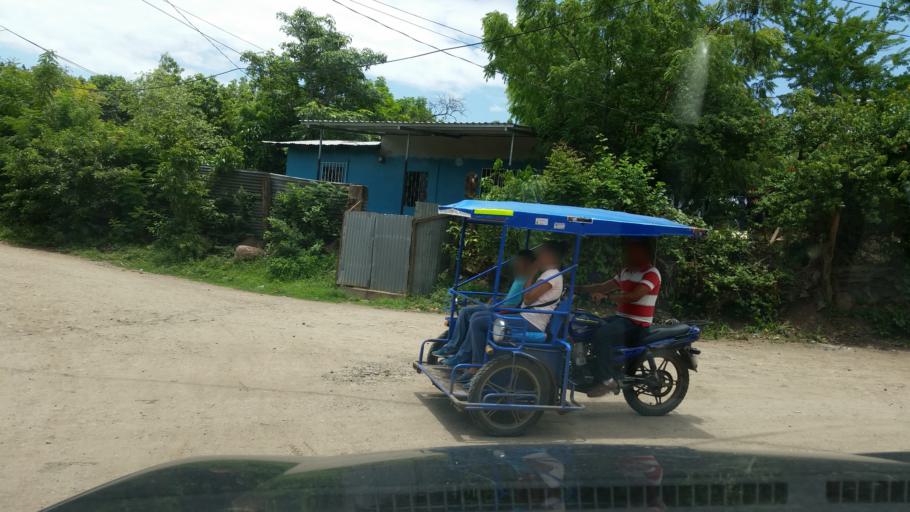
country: NI
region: Matagalpa
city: Ciudad Dario
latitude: 12.8548
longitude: -86.0926
